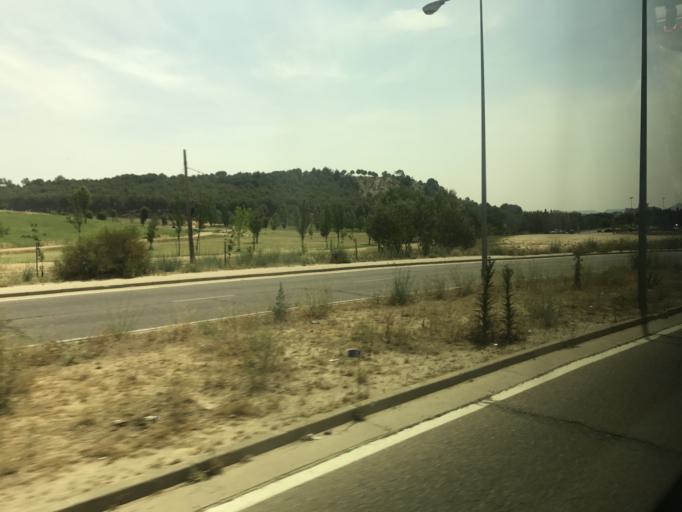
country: ES
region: Castille and Leon
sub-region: Provincia de Valladolid
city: Zaratan
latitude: 41.6507
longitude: -4.7608
